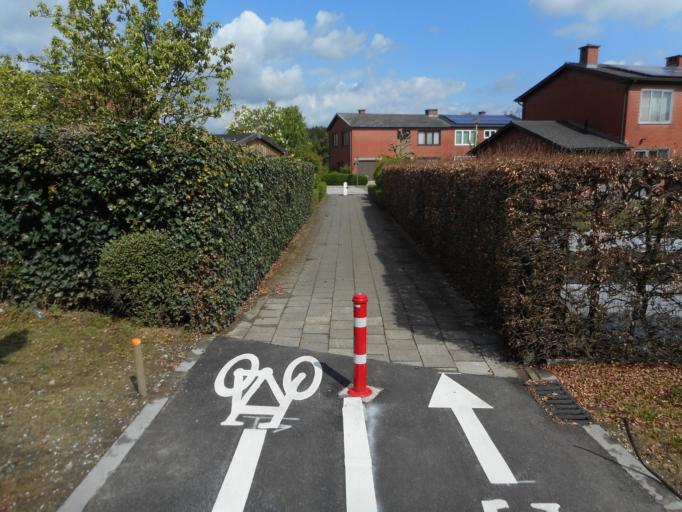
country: BE
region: Flanders
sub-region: Provincie Antwerpen
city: Puurs
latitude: 51.0782
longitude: 4.2791
